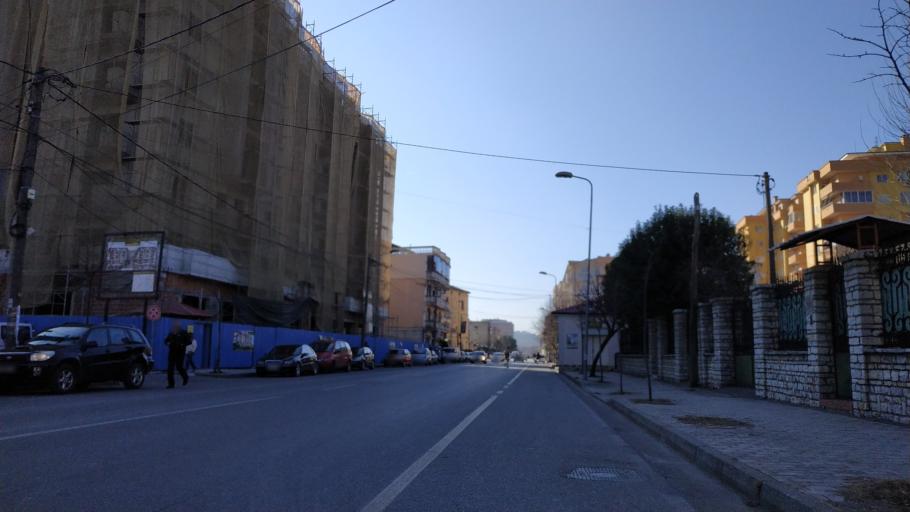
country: AL
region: Shkoder
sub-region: Rrethi i Shkodres
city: Shkoder
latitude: 42.0669
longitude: 19.5209
